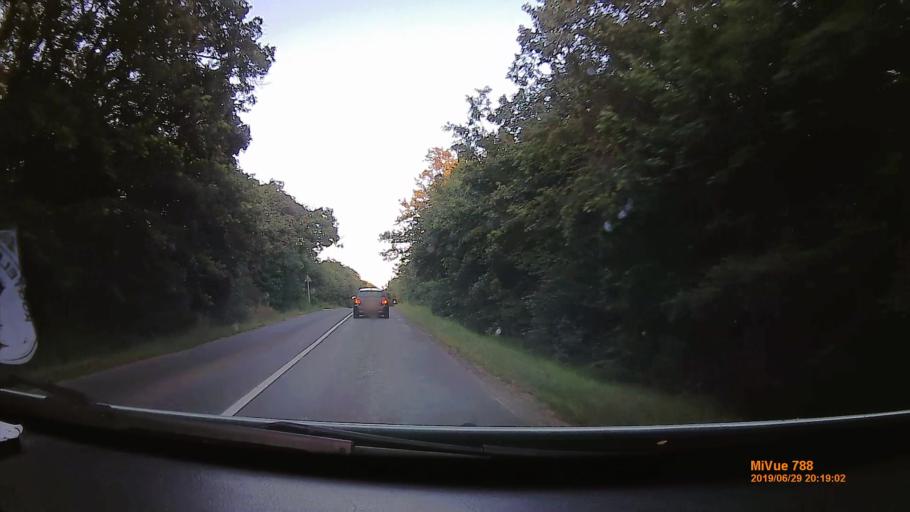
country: HU
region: Pest
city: Paty
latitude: 47.5020
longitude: 18.8623
